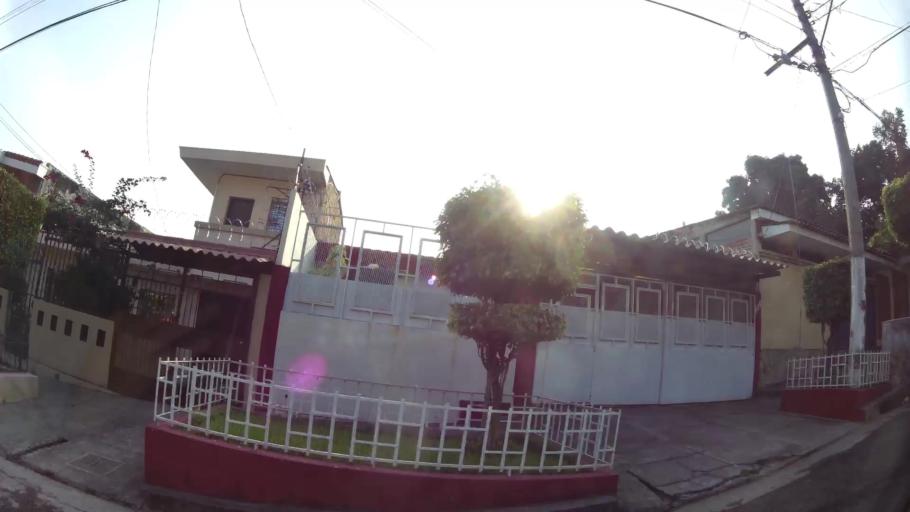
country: SV
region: San Salvador
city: San Salvador
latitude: 13.6867
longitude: -89.2045
